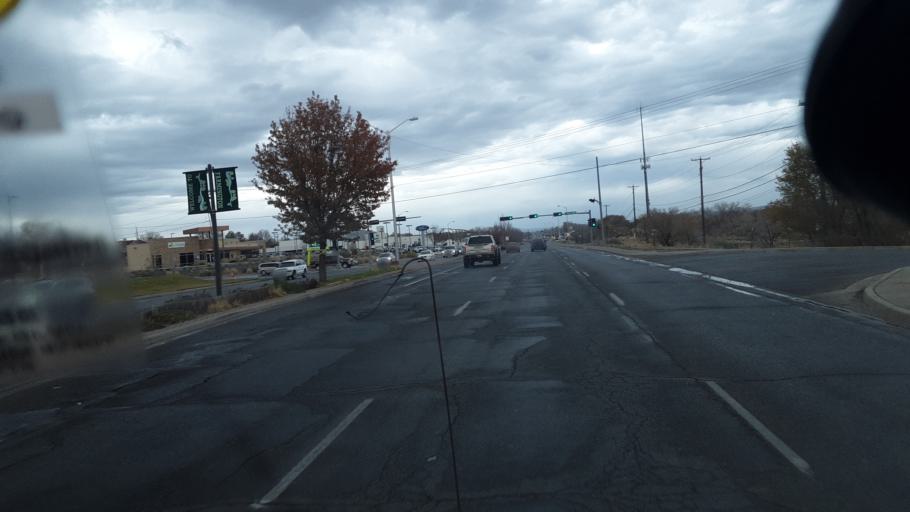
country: US
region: New Mexico
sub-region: San Juan County
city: Flora Vista
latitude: 36.7709
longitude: -108.1400
